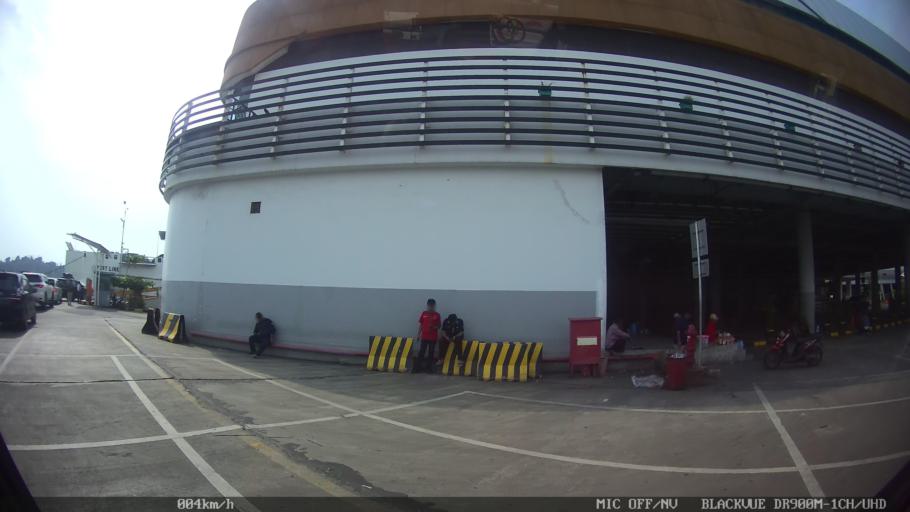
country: ID
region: Banten
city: Kubangkepuh
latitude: -5.9365
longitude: 105.9990
